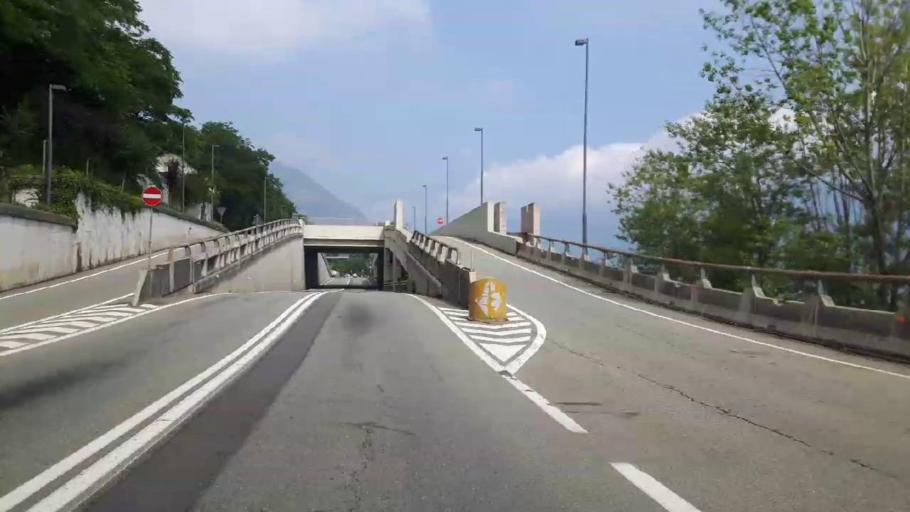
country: IT
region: Piedmont
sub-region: Provincia Verbano-Cusio-Ossola
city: Baveno
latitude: 45.9207
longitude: 8.4936
